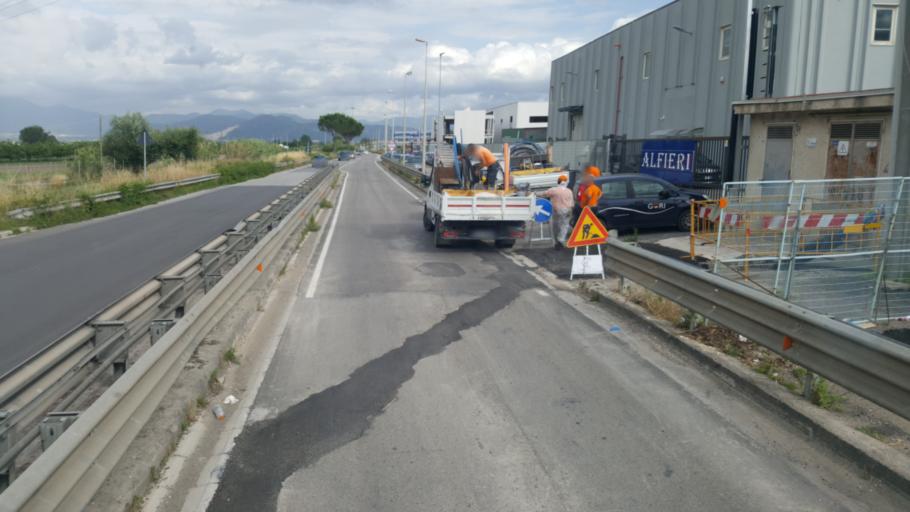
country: IT
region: Campania
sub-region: Provincia di Caserta
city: San Felice A Cancello
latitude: 40.9784
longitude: 14.4705
